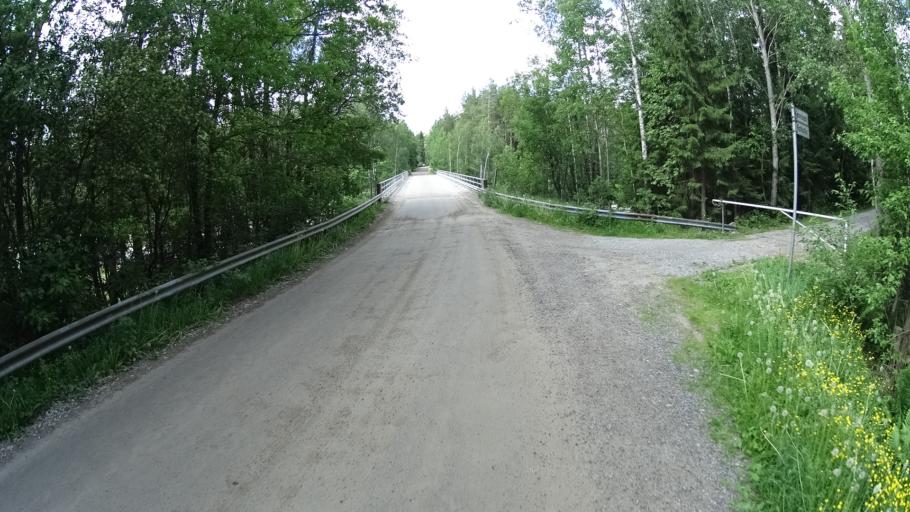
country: FI
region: Uusimaa
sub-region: Helsinki
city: Sibbo
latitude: 60.2794
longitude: 25.3156
